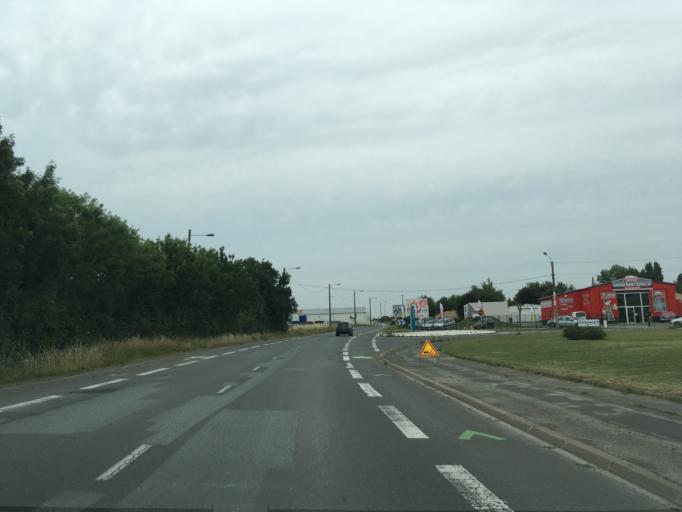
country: FR
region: Poitou-Charentes
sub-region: Departement des Deux-Sevres
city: Bessines
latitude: 46.3121
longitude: -0.4960
